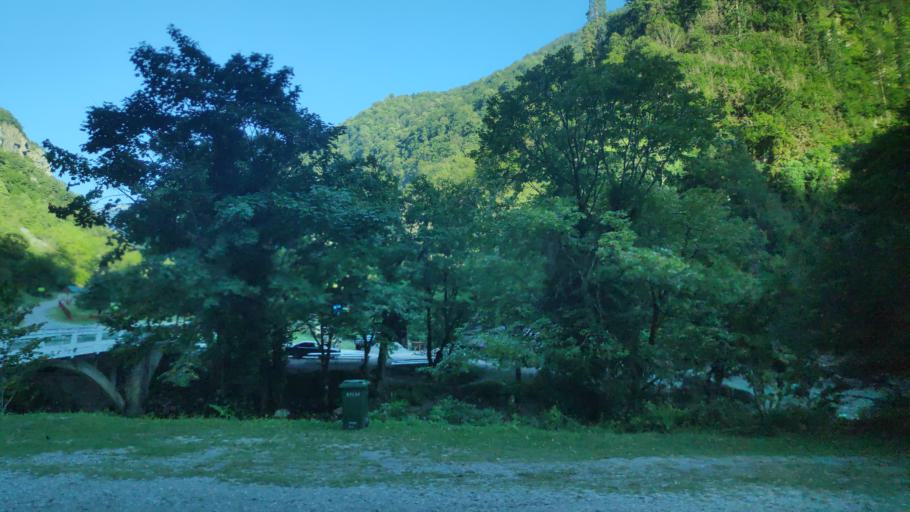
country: GE
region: Abkhazia
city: Gagra
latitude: 43.3690
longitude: 40.4579
